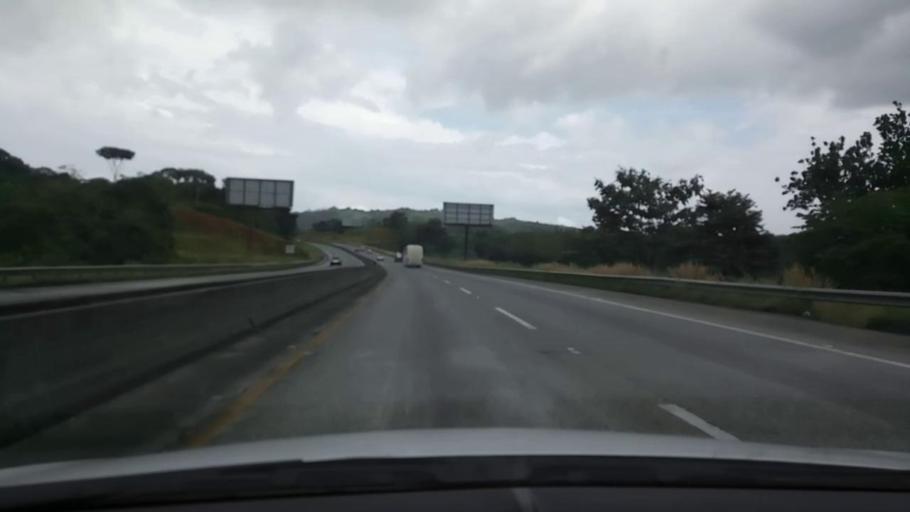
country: PA
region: Colon
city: Gatun
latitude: 9.2807
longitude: -79.7618
